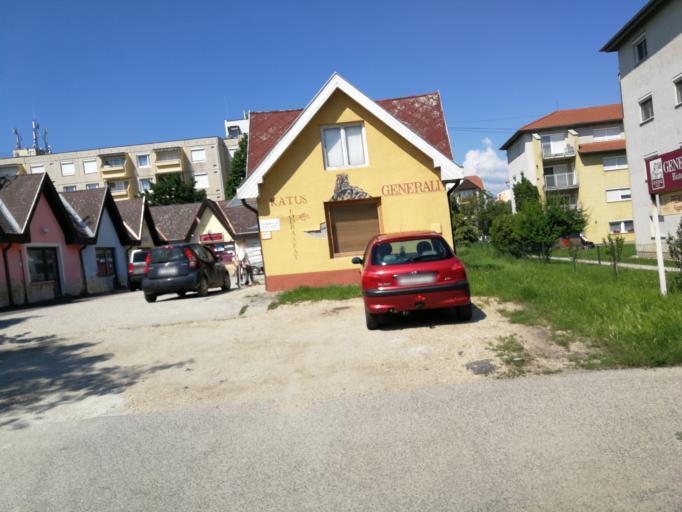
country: HU
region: Vas
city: Sarvar
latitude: 47.2549
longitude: 16.9310
